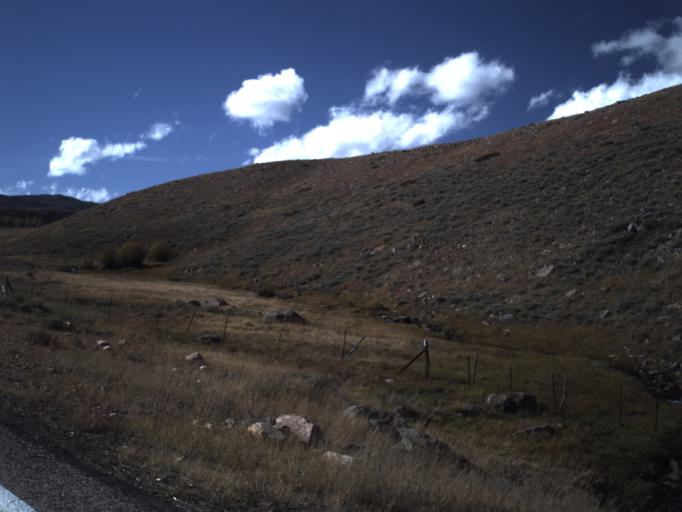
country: US
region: Utah
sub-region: Iron County
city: Parowan
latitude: 37.6647
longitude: -112.7219
